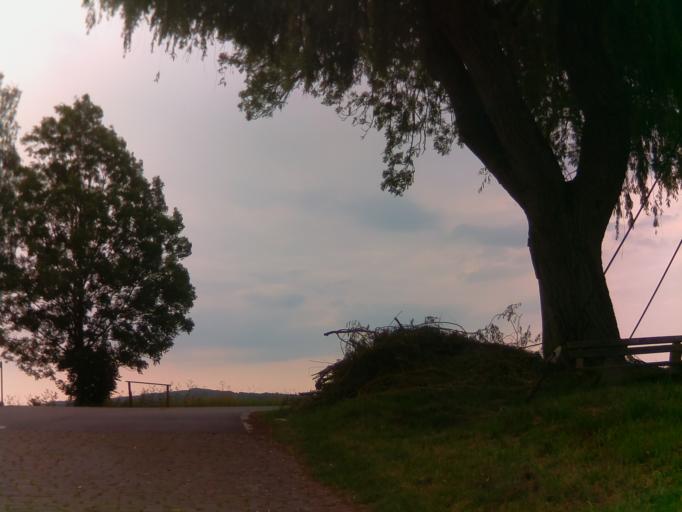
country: DE
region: Lower Saxony
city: Polle
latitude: 51.8965
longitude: 9.4092
